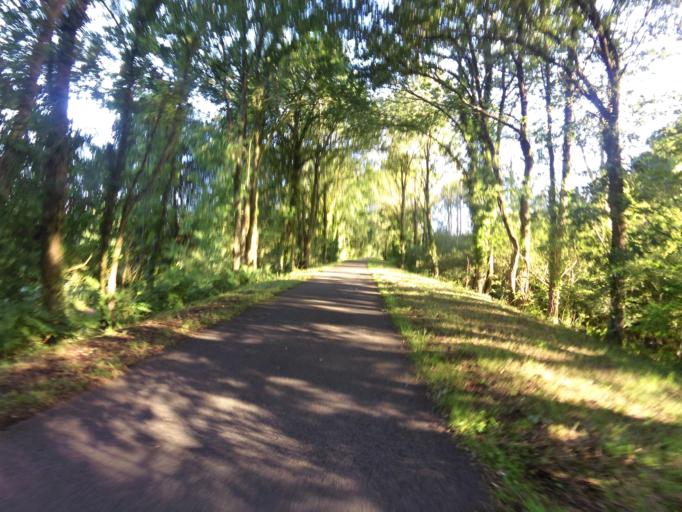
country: FR
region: Brittany
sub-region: Departement du Morbihan
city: Malestroit
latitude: 47.8432
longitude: -2.4367
